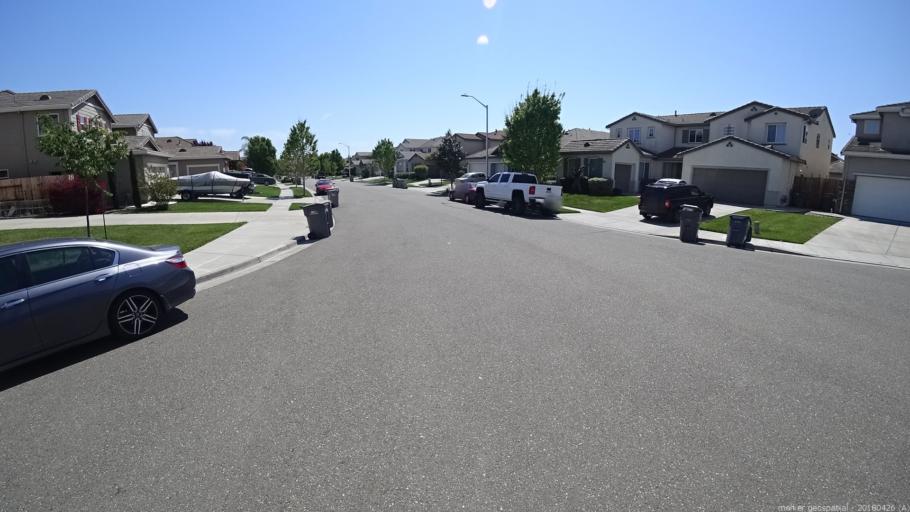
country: US
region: California
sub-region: Yolo County
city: West Sacramento
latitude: 38.5298
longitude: -121.5753
